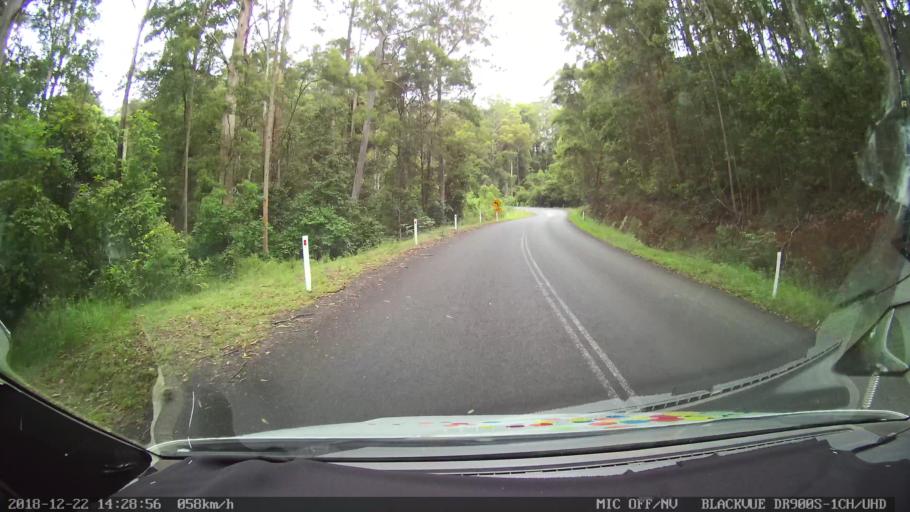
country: AU
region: New South Wales
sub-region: Bellingen
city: Dorrigo
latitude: -30.0769
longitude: 152.6368
